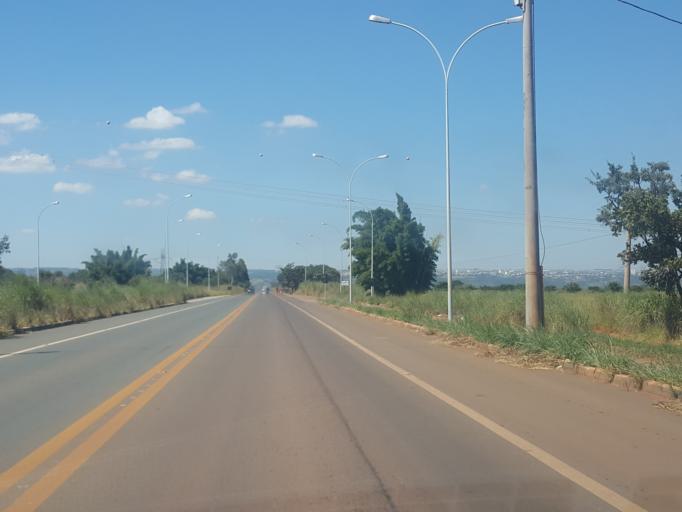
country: BR
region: Goias
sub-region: Luziania
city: Luziania
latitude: -16.0089
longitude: -48.1597
